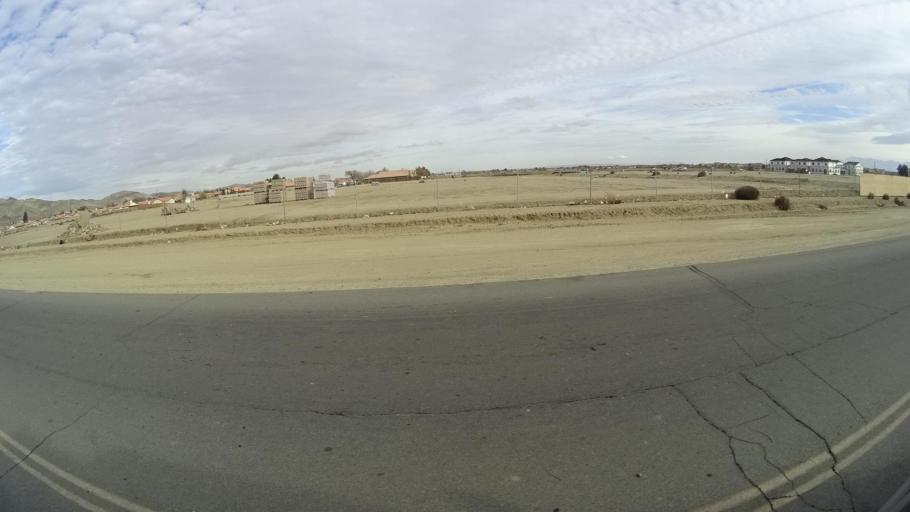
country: US
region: California
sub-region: Kern County
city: Rosamond
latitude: 34.8600
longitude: -118.1940
